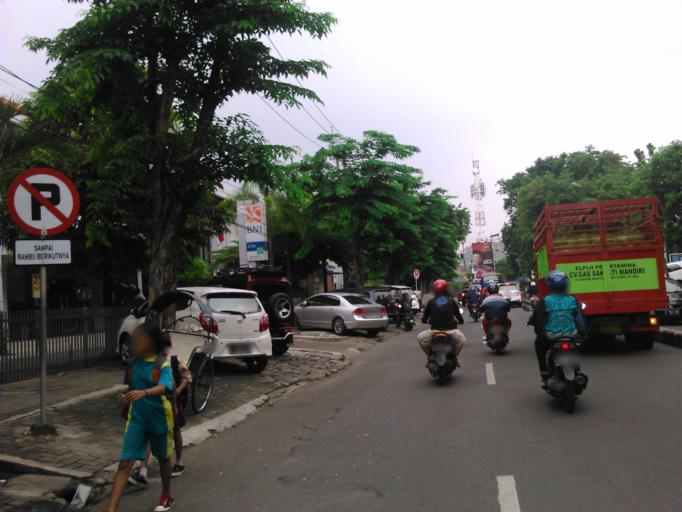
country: ID
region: East Java
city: Gubengairlangga
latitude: -7.2706
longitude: 112.7576
